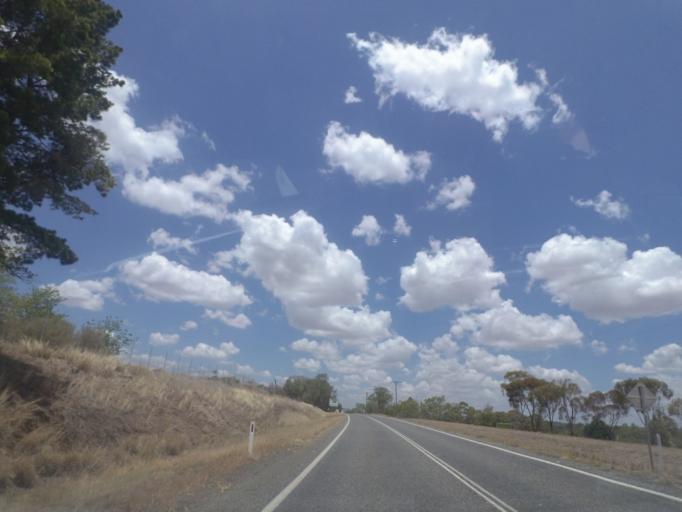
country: AU
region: Queensland
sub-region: Southern Downs
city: Warwick
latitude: -28.0274
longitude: 151.9855
